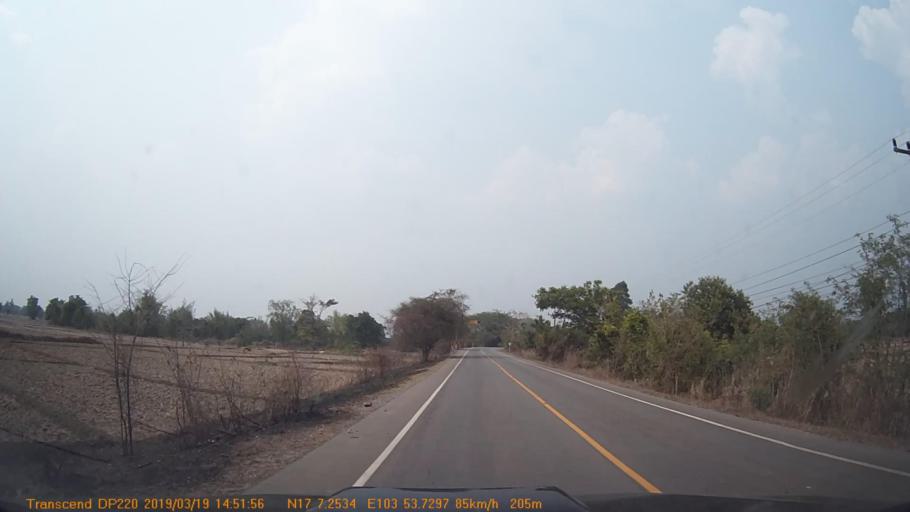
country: TH
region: Sakon Nakhon
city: Kut Bak
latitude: 17.1213
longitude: 103.8955
